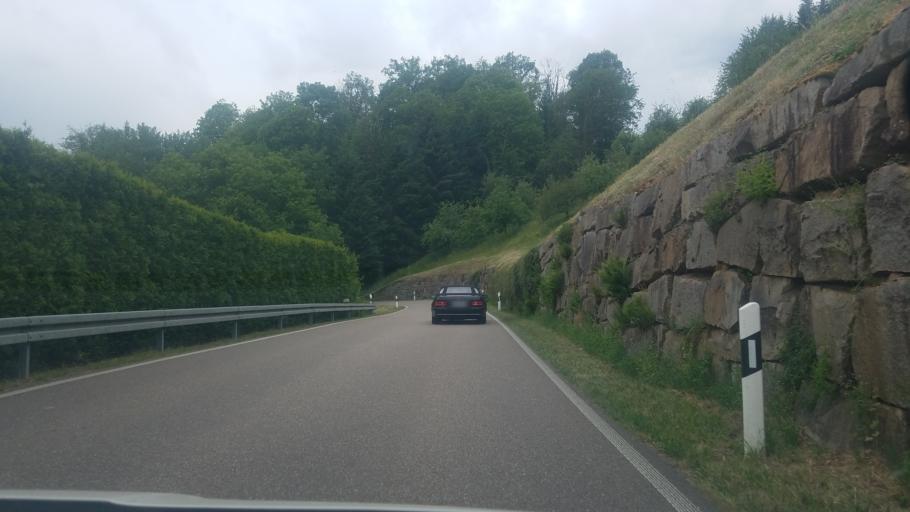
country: DE
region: Baden-Wuerttemberg
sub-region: Freiburg Region
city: Sasbachwalden
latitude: 48.6131
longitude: 8.1118
